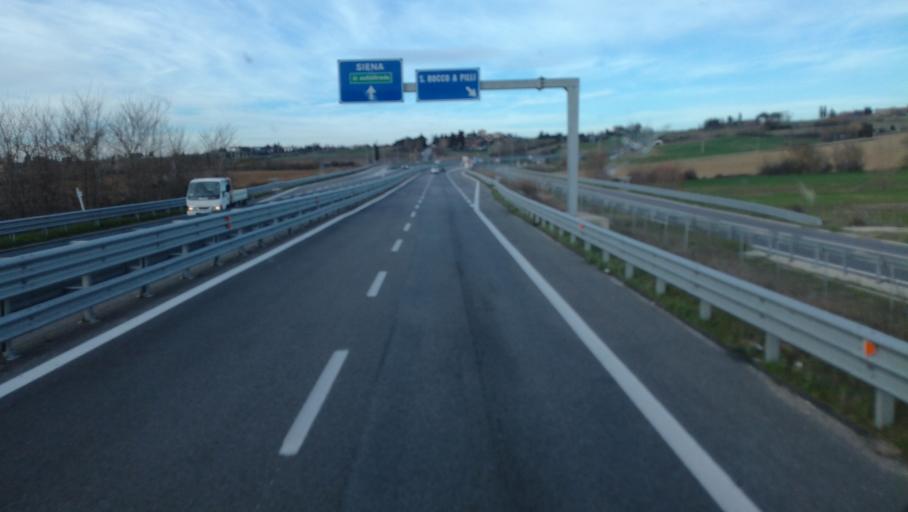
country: IT
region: Tuscany
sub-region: Provincia di Siena
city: Rosia
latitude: 43.2373
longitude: 11.2792
